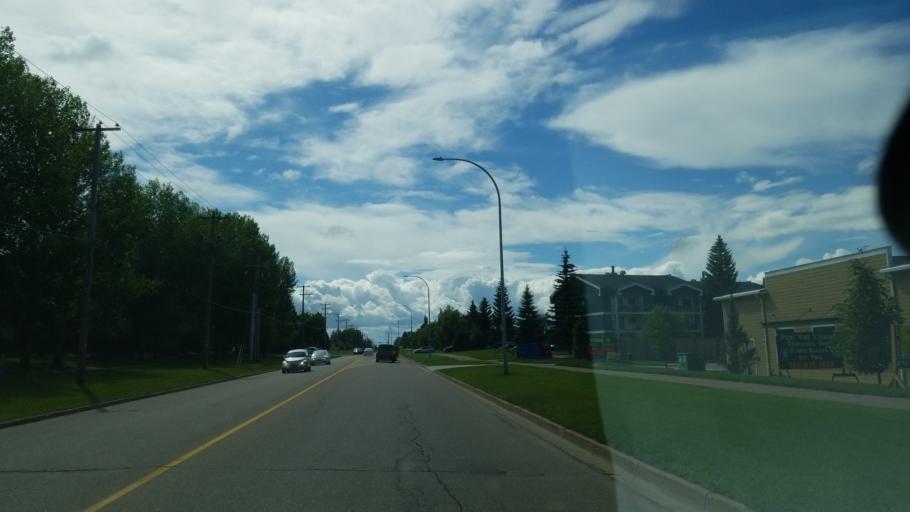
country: CA
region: Saskatchewan
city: Lloydminster
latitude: 53.2707
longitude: -110.0090
